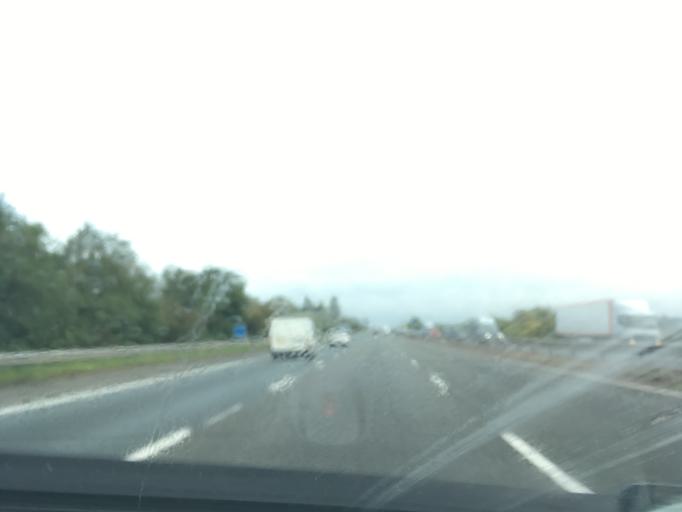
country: GB
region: England
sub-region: Oxfordshire
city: Adderbury
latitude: 52.0440
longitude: -1.3050
